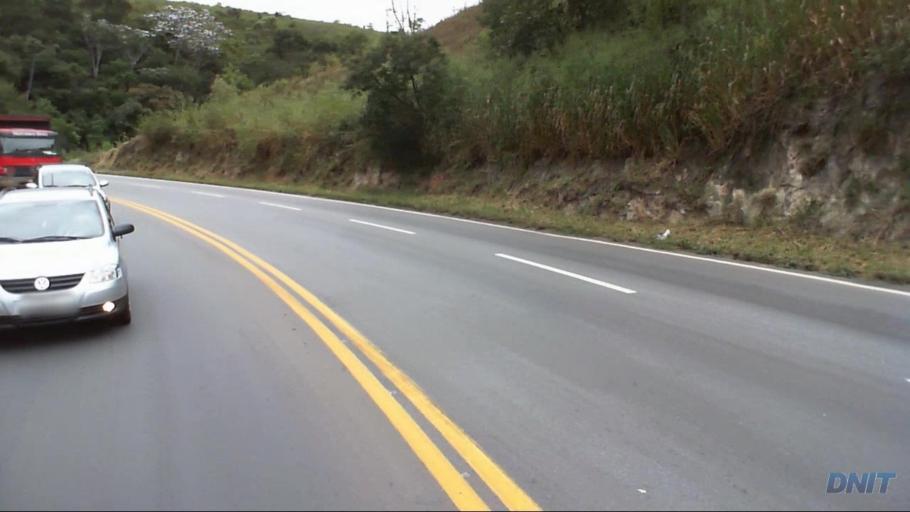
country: BR
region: Minas Gerais
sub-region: Joao Monlevade
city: Joao Monlevade
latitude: -19.8590
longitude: -43.2253
